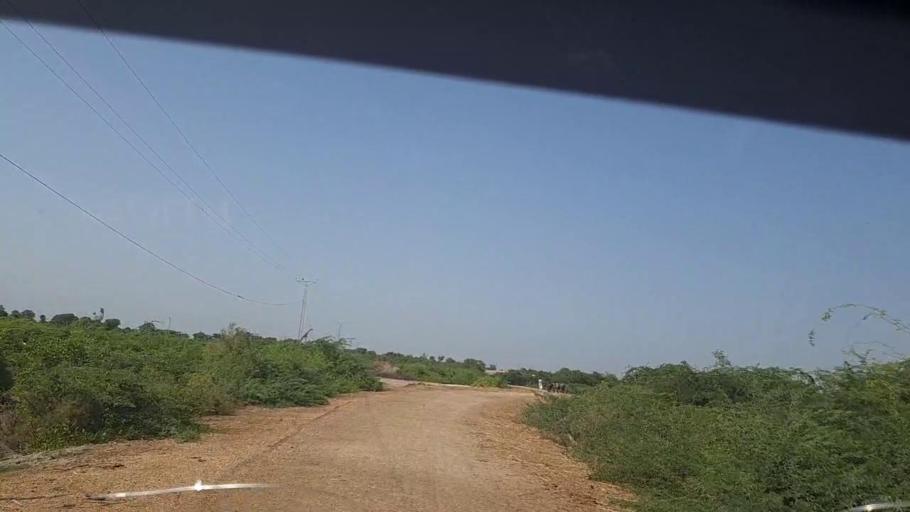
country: PK
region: Sindh
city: Rajo Khanani
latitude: 24.9560
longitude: 68.8982
